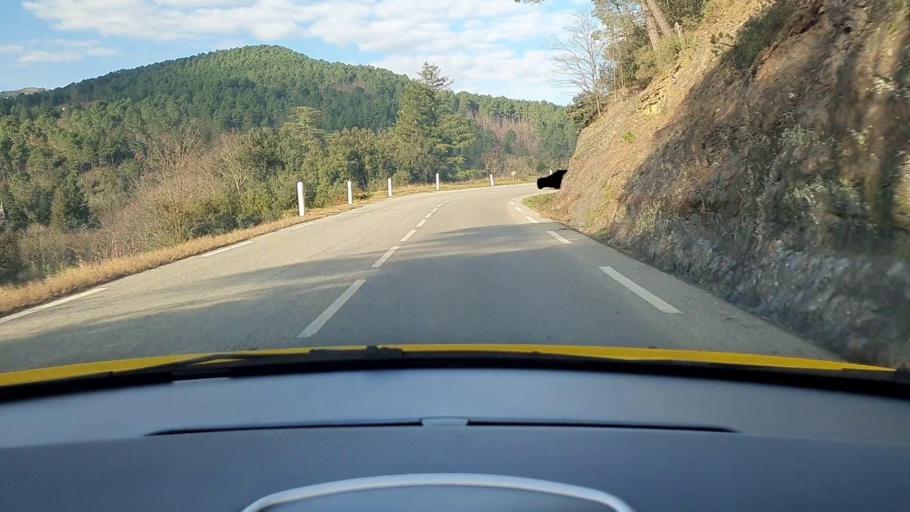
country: FR
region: Languedoc-Roussillon
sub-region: Departement du Gard
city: Branoux-les-Taillades
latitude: 44.3088
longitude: 3.9696
